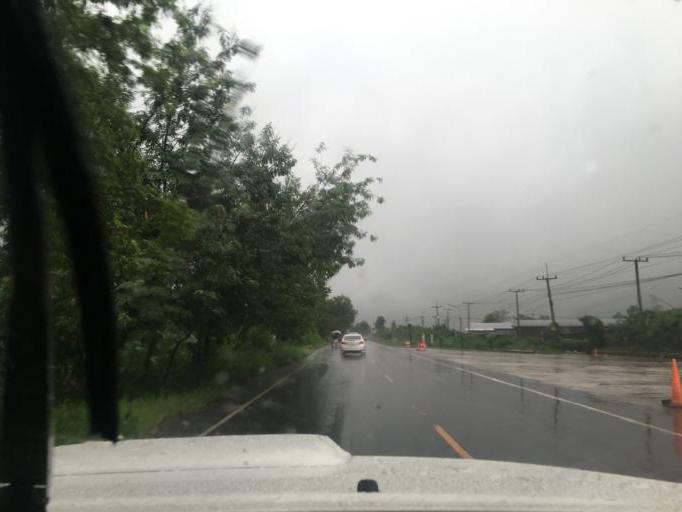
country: TH
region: Changwat Udon Thani
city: Nong Saeng
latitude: 17.2881
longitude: 102.7058
